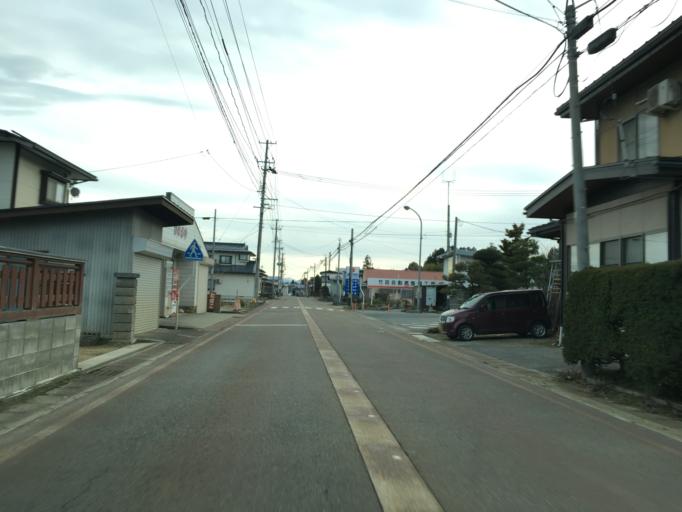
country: JP
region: Yamagata
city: Nagai
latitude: 38.1760
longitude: 140.0641
